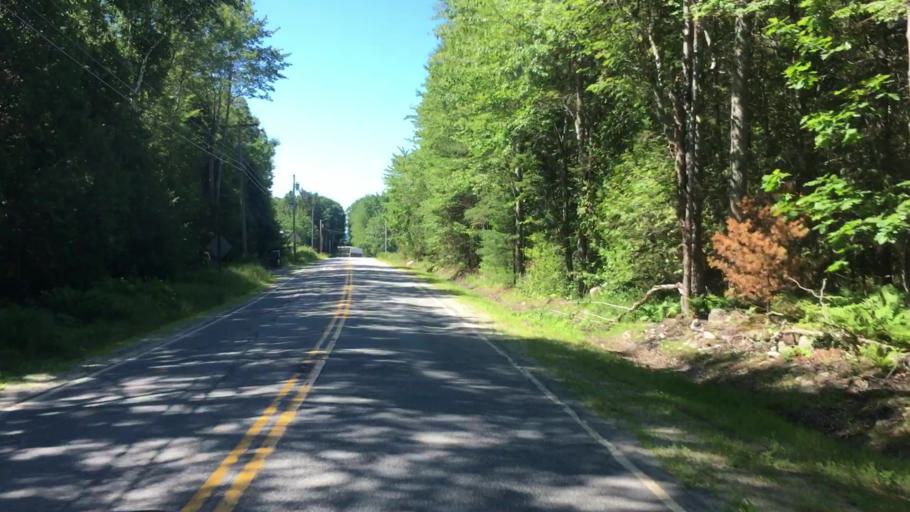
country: US
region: Maine
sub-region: Hancock County
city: Sedgwick
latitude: 44.3240
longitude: -68.6074
